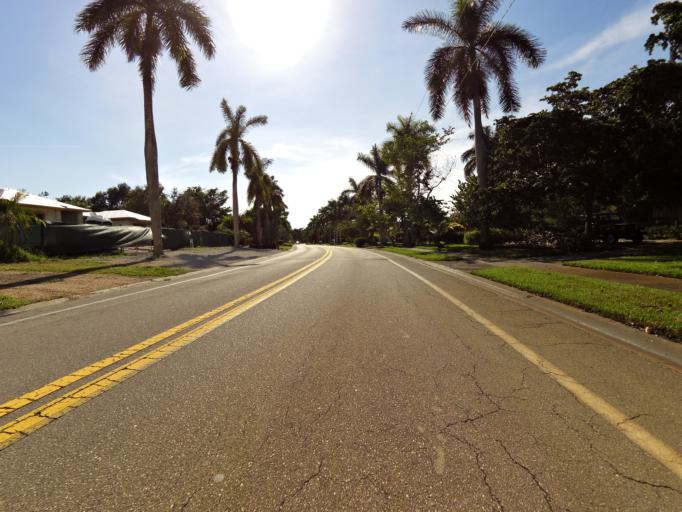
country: US
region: Florida
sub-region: Collier County
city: Naples
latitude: 26.1675
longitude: -81.8019
